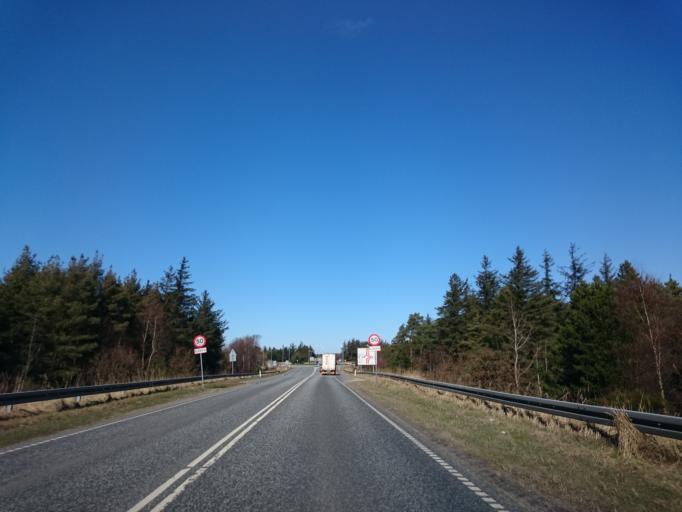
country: DK
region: North Denmark
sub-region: Frederikshavn Kommune
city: Skagen
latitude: 57.6552
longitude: 10.4585
